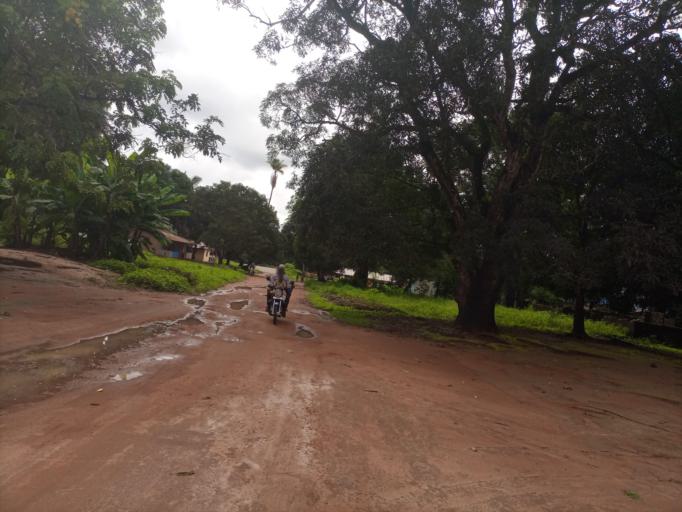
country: SL
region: Northern Province
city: Sawkta
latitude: 8.6378
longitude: -13.1905
